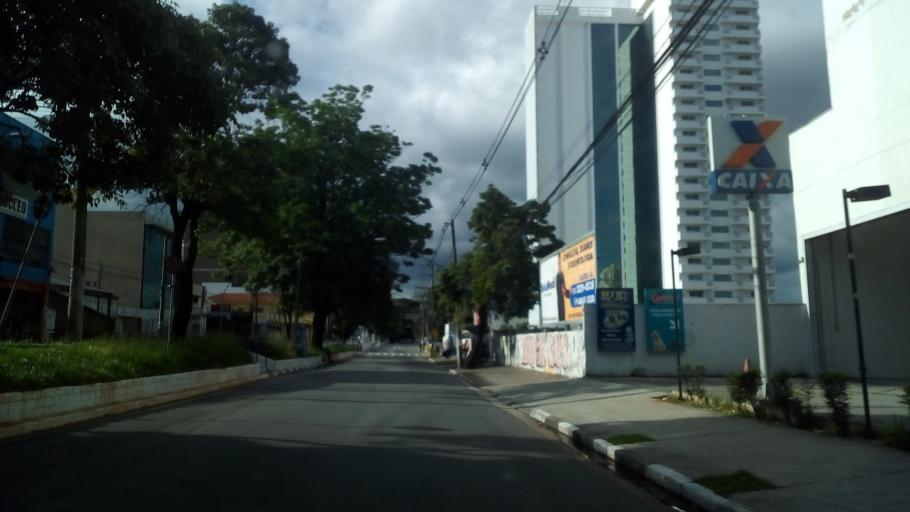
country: BR
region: Sao Paulo
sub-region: Guarulhos
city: Guarulhos
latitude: -23.4642
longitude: -46.5303
